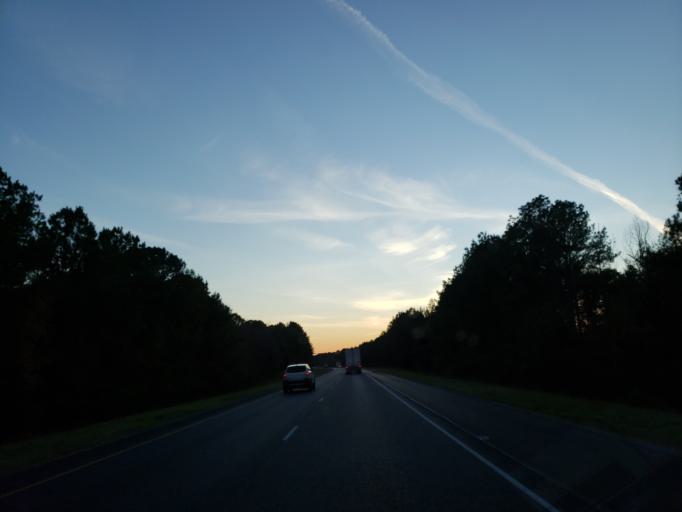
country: US
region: Alabama
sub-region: Sumter County
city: Livingston
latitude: 32.5702
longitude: -88.2494
